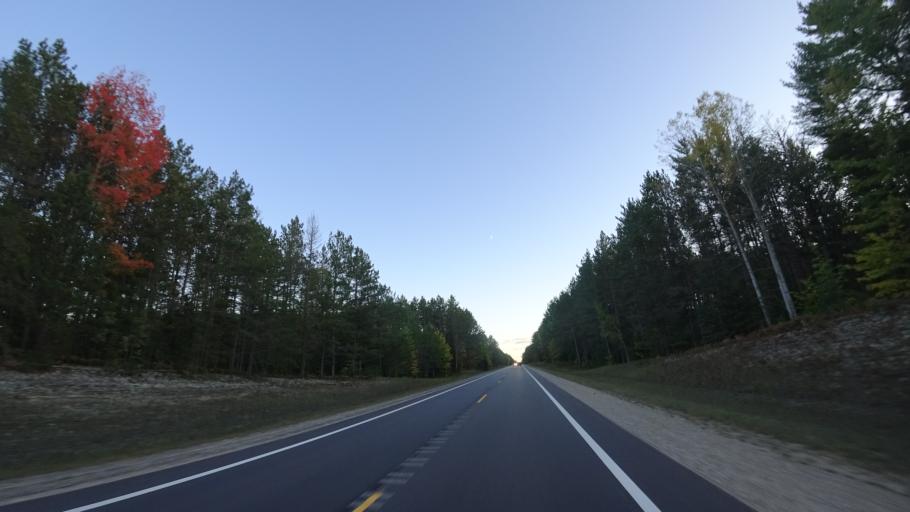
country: US
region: Michigan
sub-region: Luce County
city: Newberry
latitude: 46.3222
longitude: -85.0093
